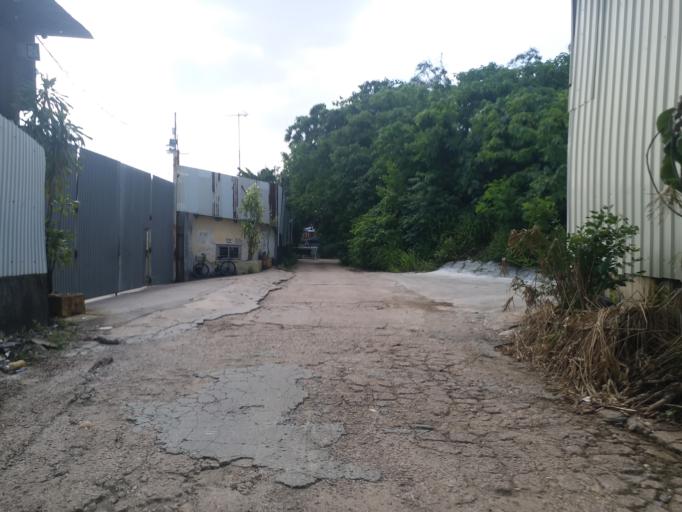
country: HK
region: Yuen Long
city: Yuen Long Kau Hui
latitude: 22.4415
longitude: 114.0015
